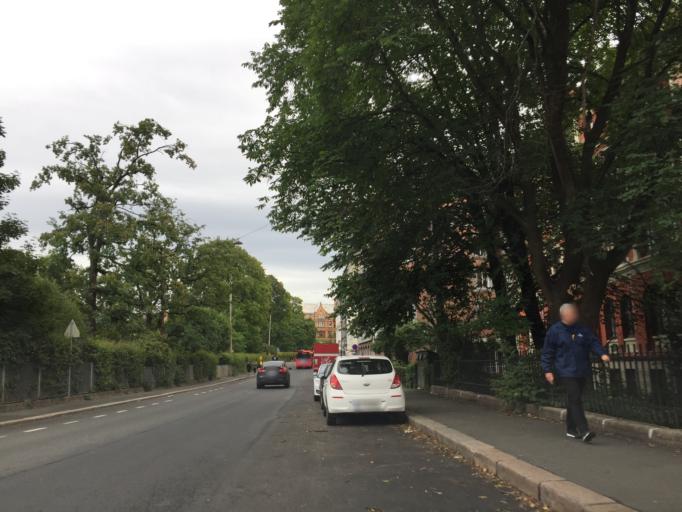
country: NO
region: Oslo
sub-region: Oslo
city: Oslo
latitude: 59.9210
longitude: 10.7421
